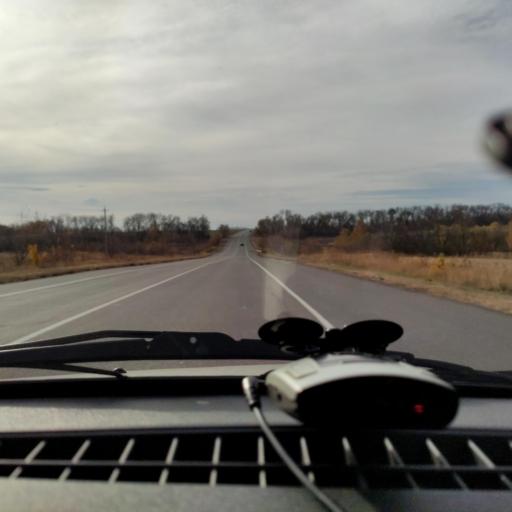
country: RU
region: Voronezj
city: Devitsa
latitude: 51.5747
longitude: 38.9749
